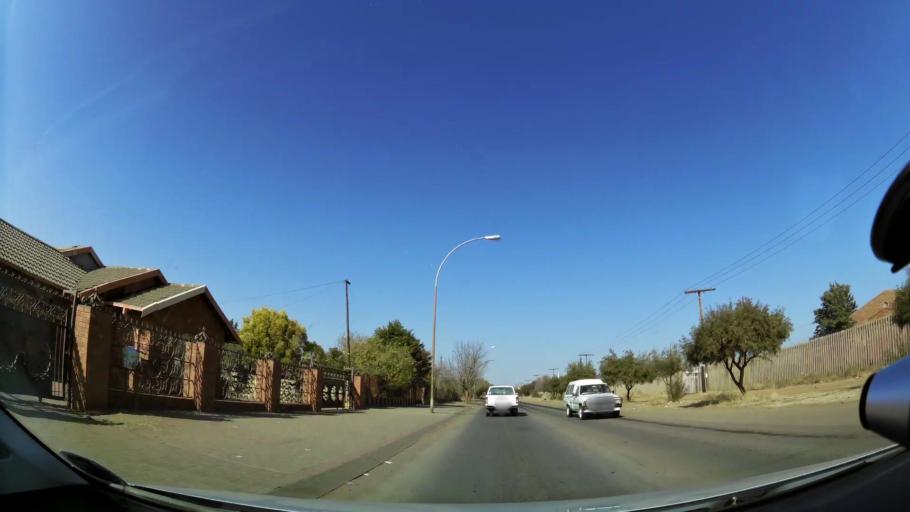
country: ZA
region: Orange Free State
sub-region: Mangaung Metropolitan Municipality
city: Bloemfontein
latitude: -29.1890
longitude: 26.2217
